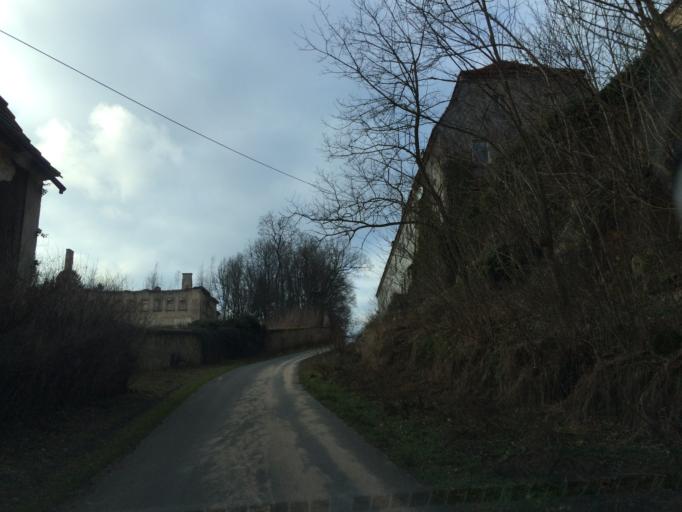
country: PL
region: Lower Silesian Voivodeship
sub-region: Powiat lwowecki
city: Lwowek Slaski
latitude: 51.1588
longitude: 15.5936
